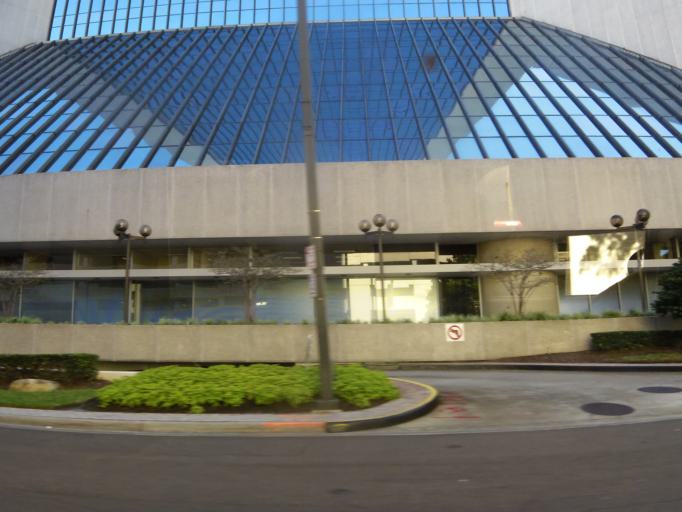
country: US
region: Florida
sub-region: Duval County
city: Jacksonville
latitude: 30.3262
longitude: -81.6587
